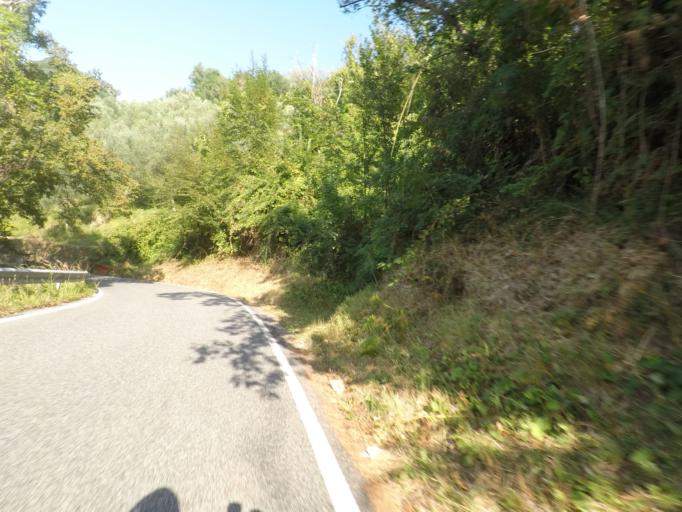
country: IT
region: Liguria
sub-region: Provincia di La Spezia
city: Casano-Dogana-Isola
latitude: 44.0840
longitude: 10.0508
